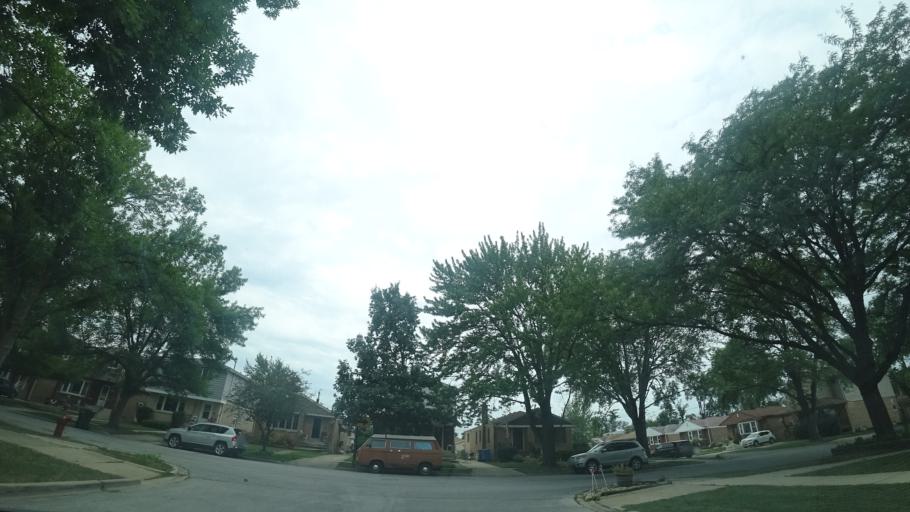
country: US
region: Illinois
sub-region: Cook County
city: Merrionette Park
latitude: 41.6979
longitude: -87.7182
